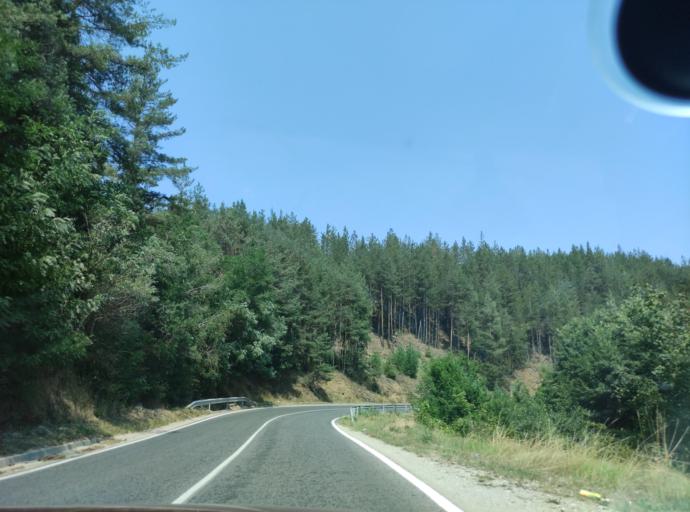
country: BG
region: Blagoevgrad
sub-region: Obshtina Razlog
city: Razlog
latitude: 41.8927
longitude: 23.5355
